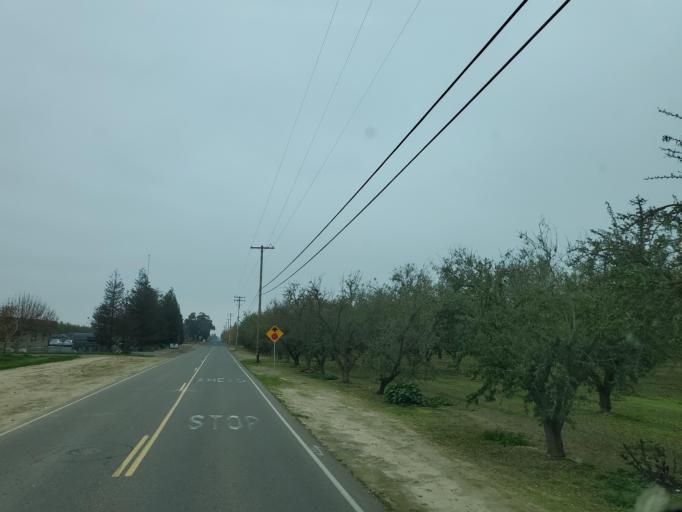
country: US
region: California
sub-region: Stanislaus County
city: Hughson
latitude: 37.5892
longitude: -120.8700
